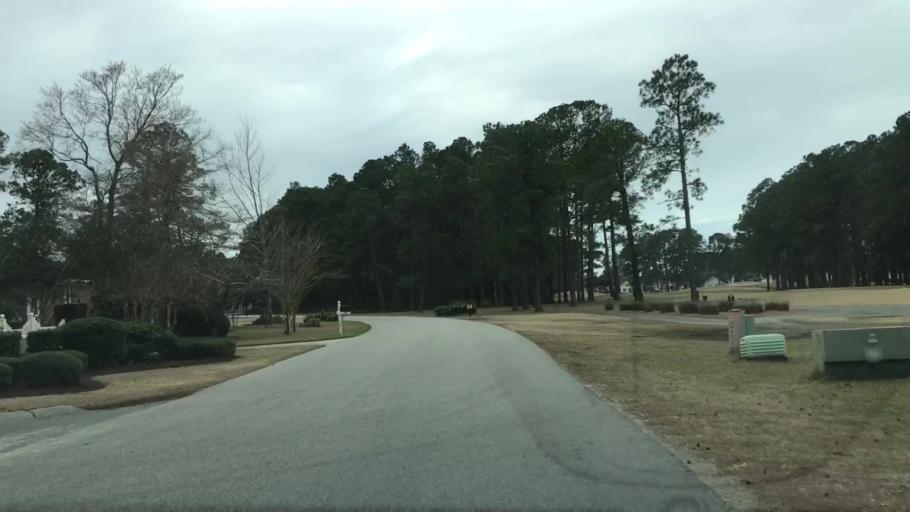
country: US
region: South Carolina
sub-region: Horry County
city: Red Hill
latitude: 33.7750
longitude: -79.0035
